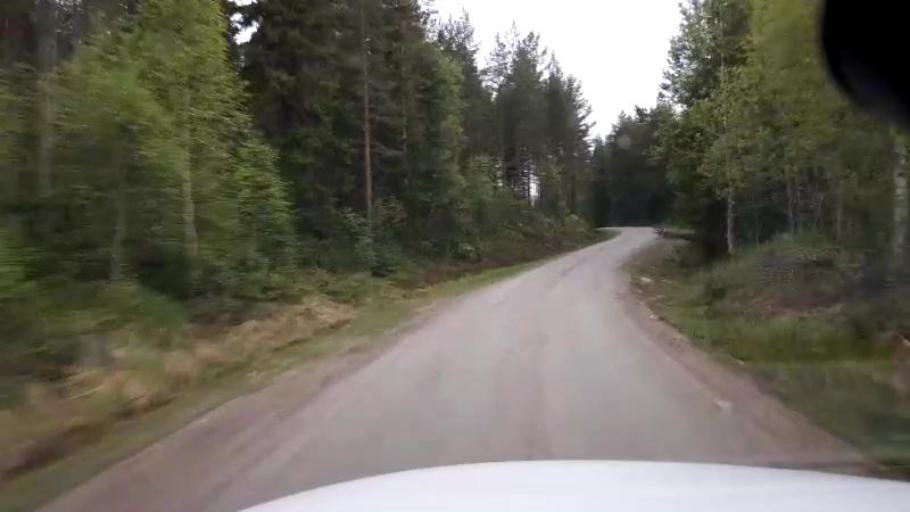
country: SE
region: Gaevleborg
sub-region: Ljusdals Kommun
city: Jaervsoe
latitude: 61.7671
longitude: 16.1865
